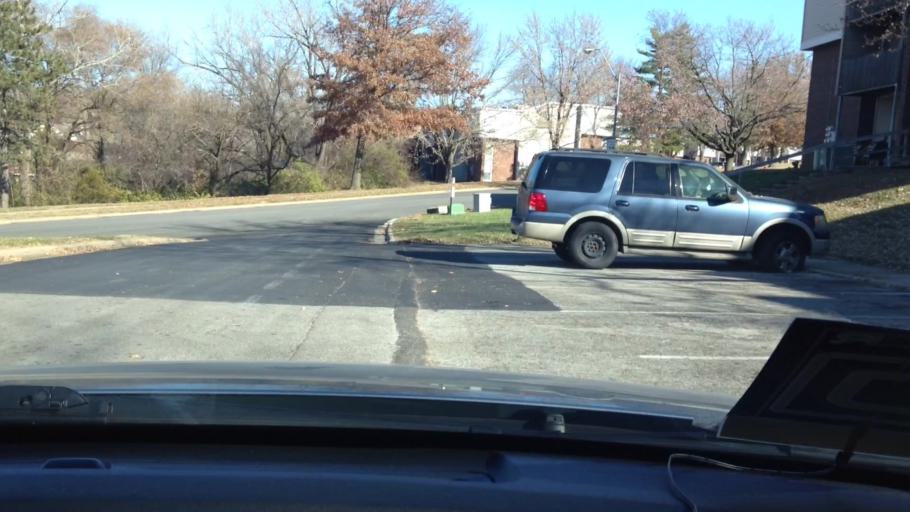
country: US
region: Missouri
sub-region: Jackson County
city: Raytown
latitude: 39.0461
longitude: -94.4559
